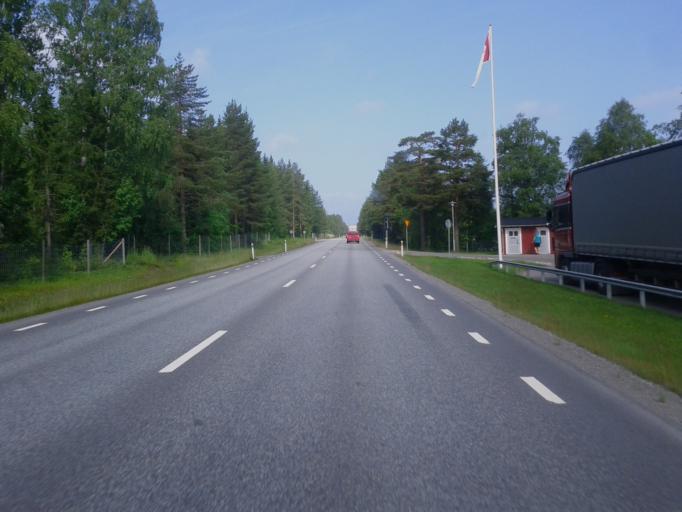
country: SE
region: Vaesterbotten
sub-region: Skelleftea Kommun
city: Burea
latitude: 64.5389
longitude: 21.2563
